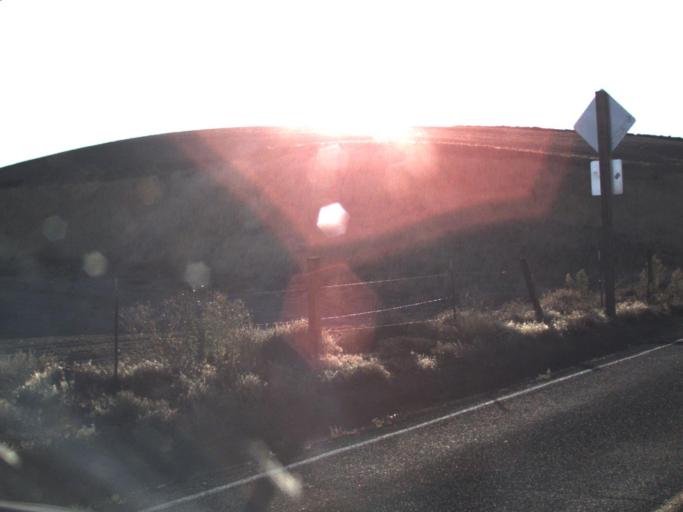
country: US
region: Washington
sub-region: Walla Walla County
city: Waitsburg
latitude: 46.6773
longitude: -118.3448
